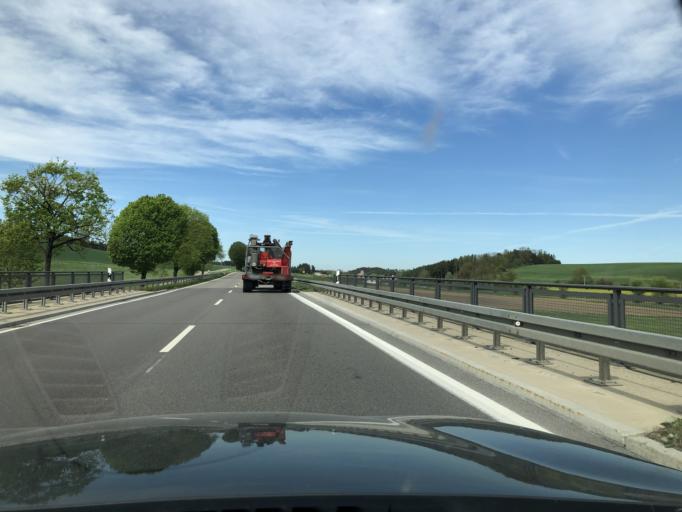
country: DE
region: Bavaria
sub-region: Swabia
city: Laugna
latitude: 48.5407
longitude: 10.7347
